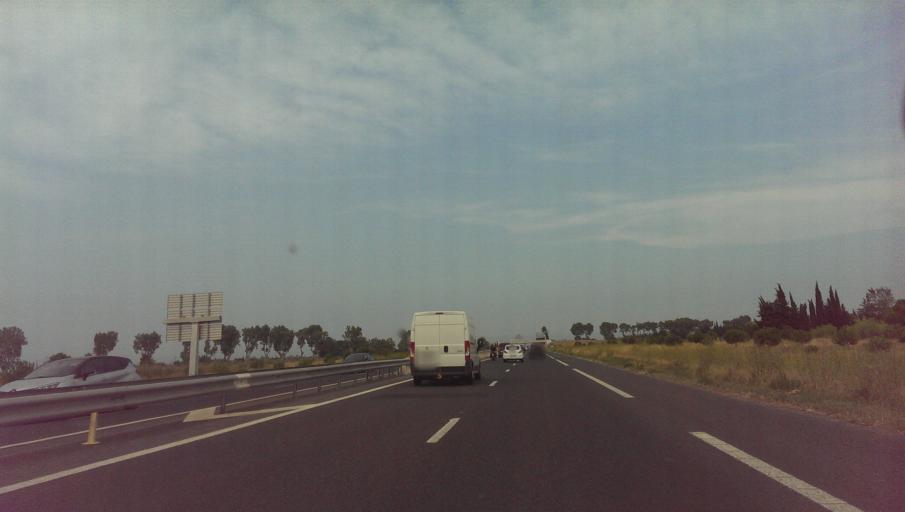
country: FR
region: Languedoc-Roussillon
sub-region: Departement des Pyrenees-Orientales
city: Saint-Hippolyte
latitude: 42.7795
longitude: 2.9719
